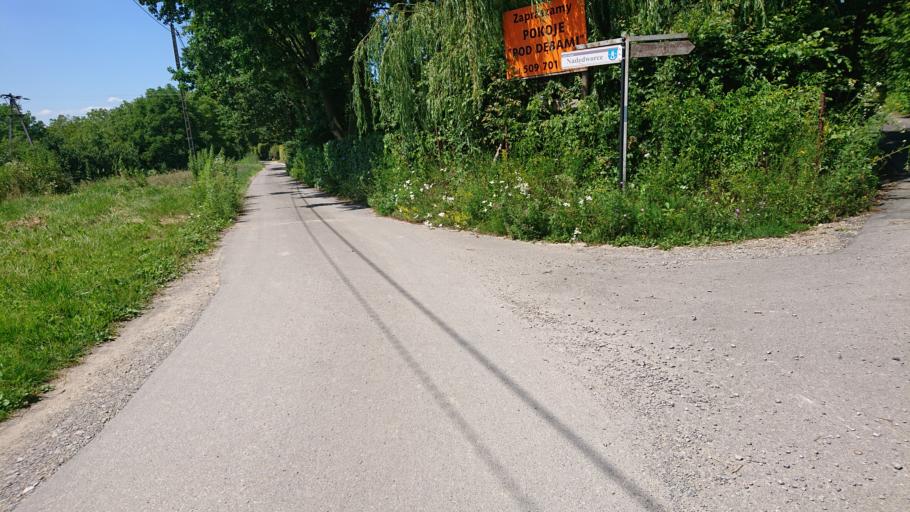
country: PL
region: Lublin Voivodeship
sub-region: Powiat pulawski
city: Kazimierz Dolny
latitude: 51.3267
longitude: 21.9691
